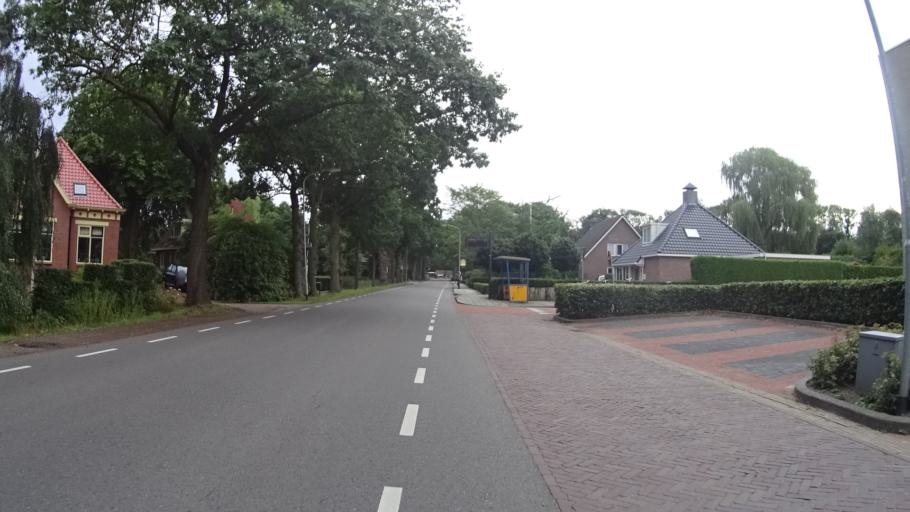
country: NL
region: Groningen
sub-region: Gemeente Slochteren
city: Slochteren
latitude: 53.2203
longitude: 6.8056
